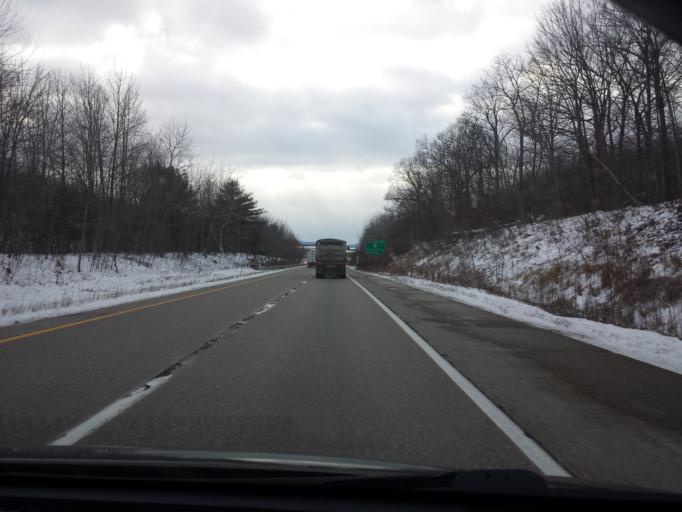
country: US
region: Pennsylvania
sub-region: Luzerne County
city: Conyngham
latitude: 41.0311
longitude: -76.0691
